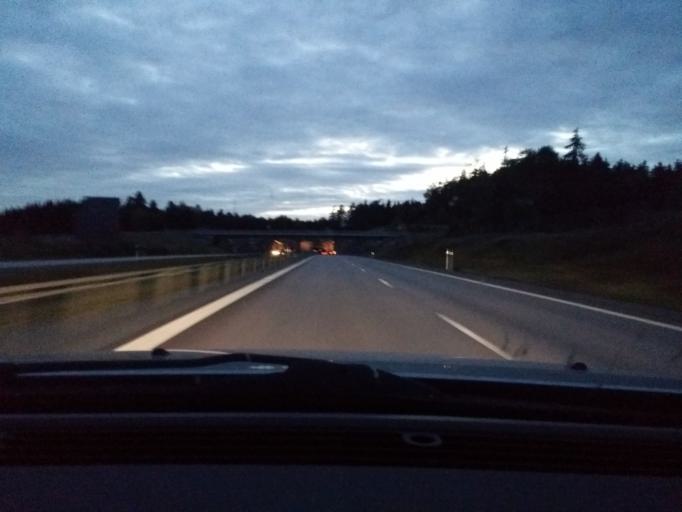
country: SE
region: Uppsala
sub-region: Enkopings Kommun
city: Enkoping
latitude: 59.6451
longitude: 17.0308
